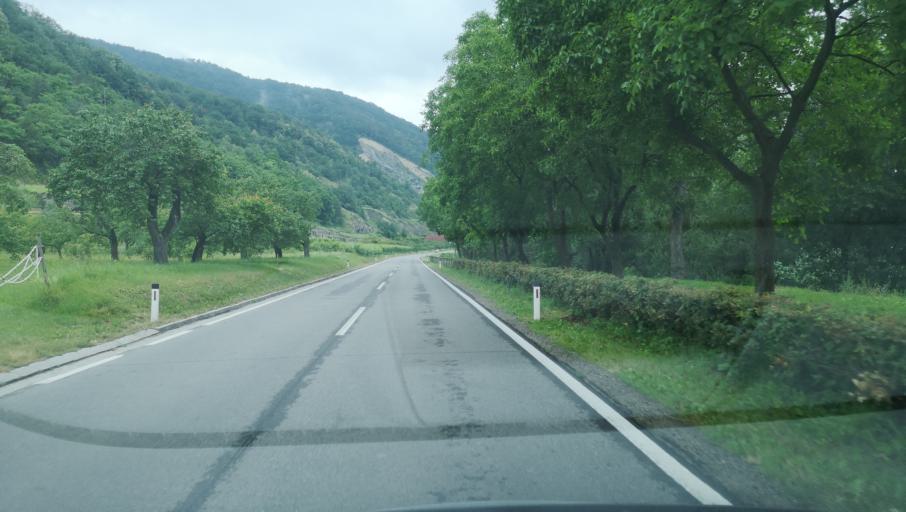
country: AT
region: Lower Austria
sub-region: Politischer Bezirk Krems
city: Spitz
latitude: 48.3424
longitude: 15.4049
